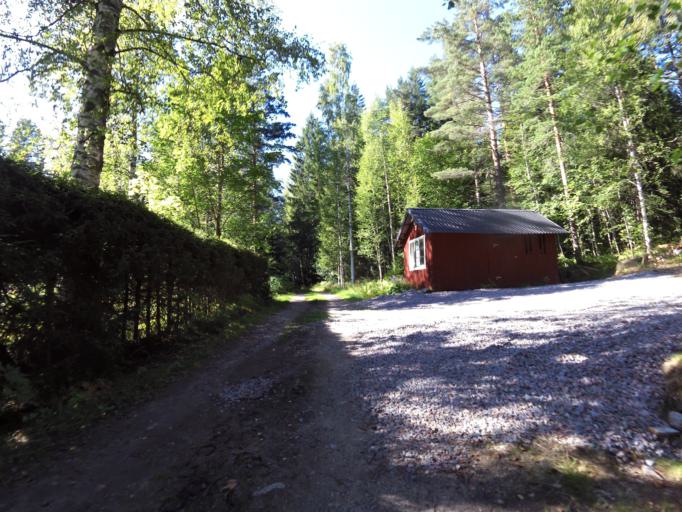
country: SE
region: Gaevleborg
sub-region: Hofors Kommun
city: Hofors
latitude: 60.5811
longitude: 16.4069
